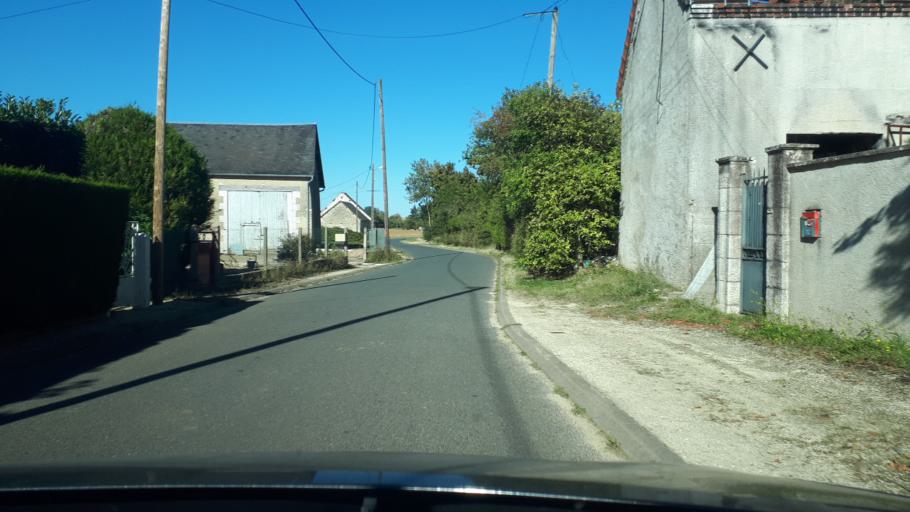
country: FR
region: Centre
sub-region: Departement du Cher
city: Baugy
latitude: 47.2039
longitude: 2.7364
